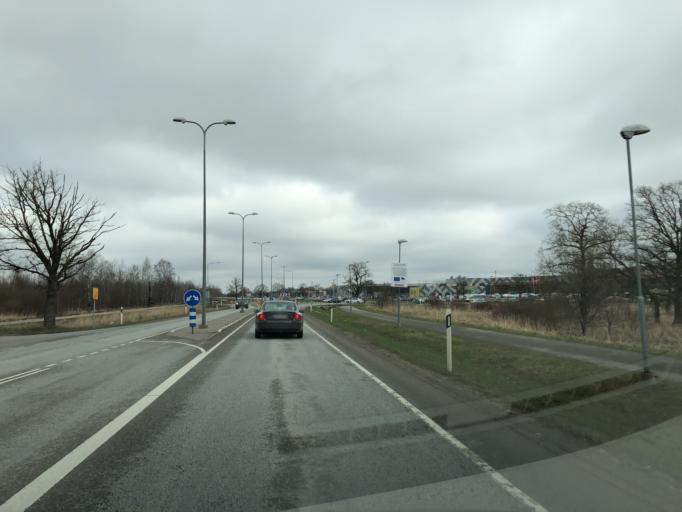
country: EE
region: Laeaene-Virumaa
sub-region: Rakvere linn
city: Rakvere
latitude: 59.3620
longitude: 26.3353
